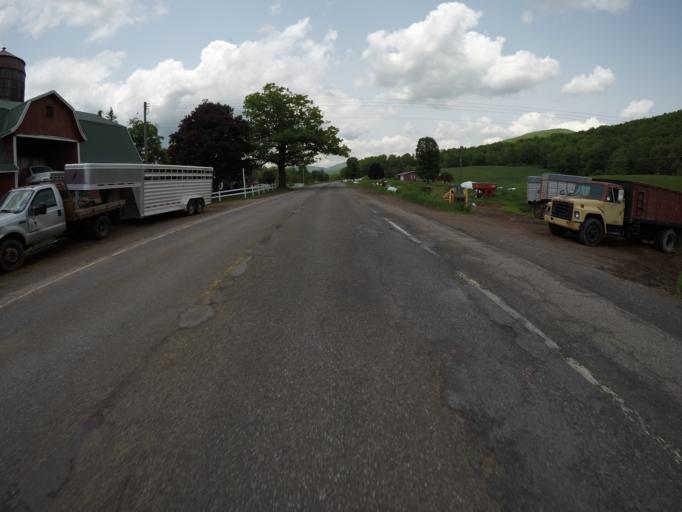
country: US
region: New York
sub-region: Delaware County
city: Stamford
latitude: 42.2394
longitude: -74.5996
